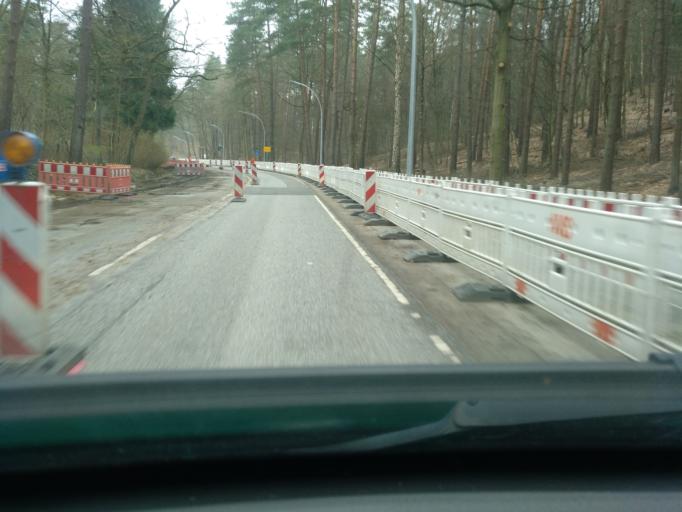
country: DE
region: Hamburg
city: Harburg
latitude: 53.4582
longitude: 9.8935
